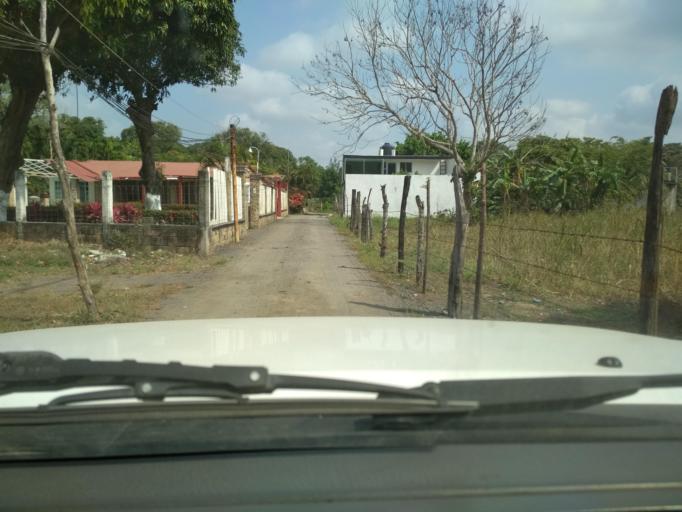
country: MX
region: Veracruz
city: El Tejar
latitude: 19.0765
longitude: -96.1662
